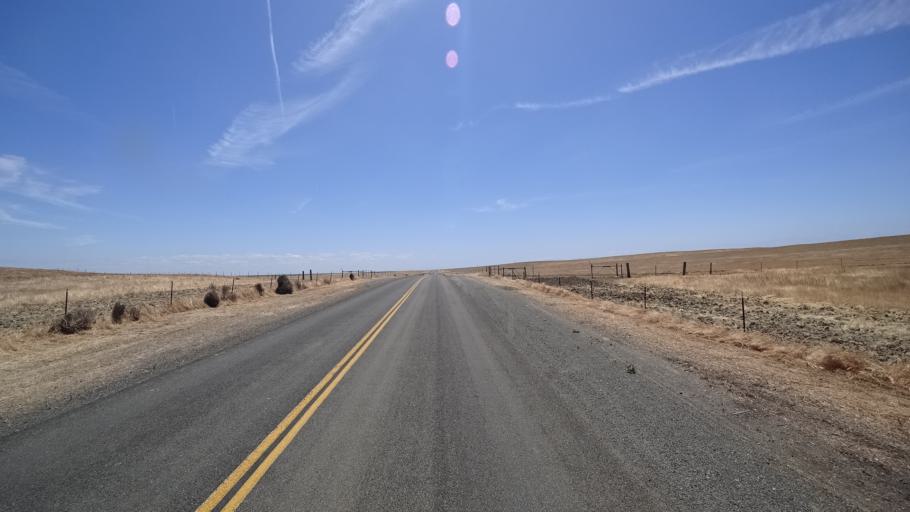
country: US
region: California
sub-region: Kings County
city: Kettleman City
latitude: 35.8184
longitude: -119.9049
